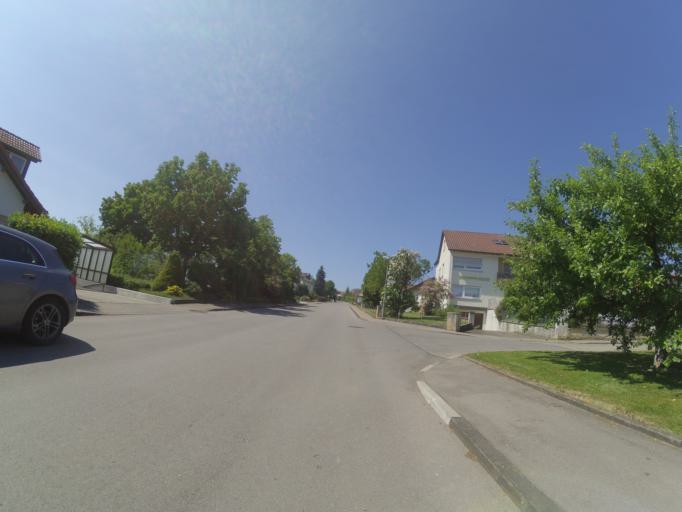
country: DE
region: Baden-Wuerttemberg
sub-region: Tuebingen Region
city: Merklingen
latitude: 48.5058
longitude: 9.7574
